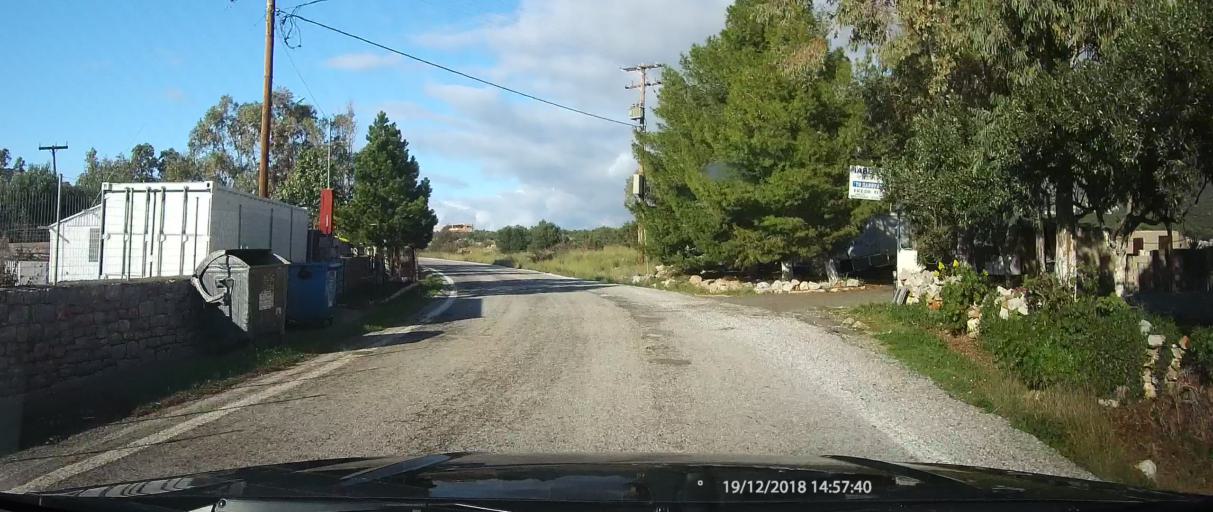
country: GR
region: Peloponnese
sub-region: Nomos Lakonias
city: Gytheio
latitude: 36.4812
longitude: 22.4052
